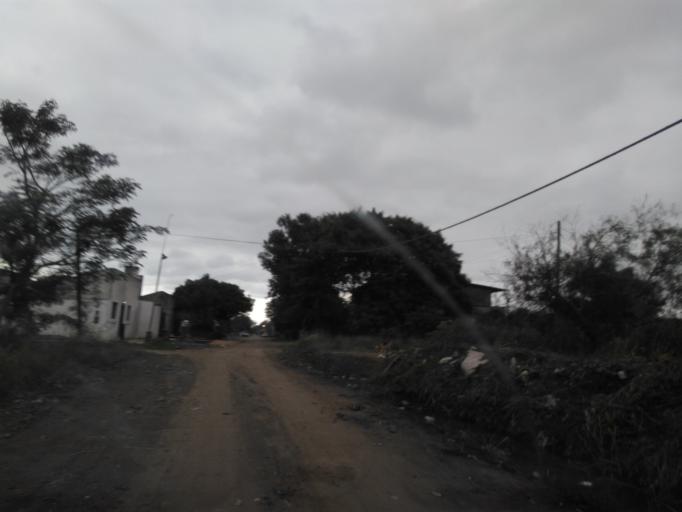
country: AR
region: Chaco
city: Fontana
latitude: -27.4480
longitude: -59.0303
